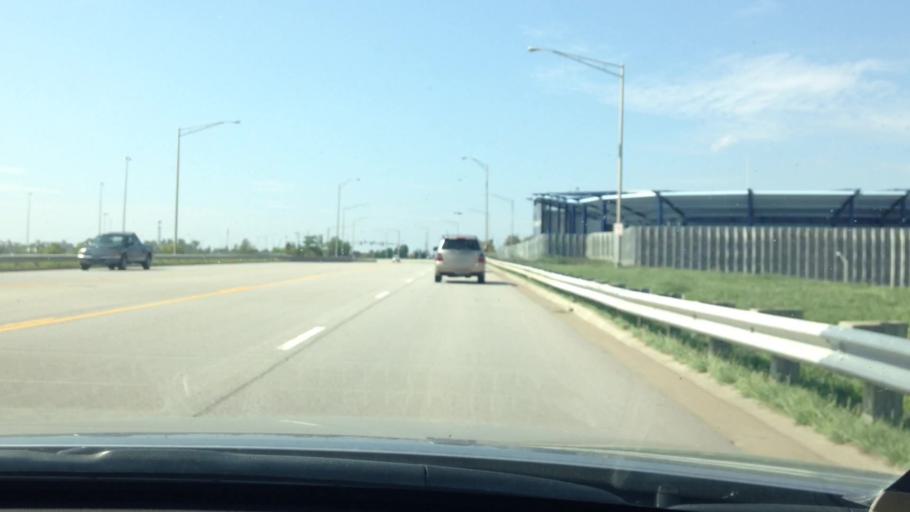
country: US
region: Kansas
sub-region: Wyandotte County
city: Edwardsville
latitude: 39.1194
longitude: -94.8227
